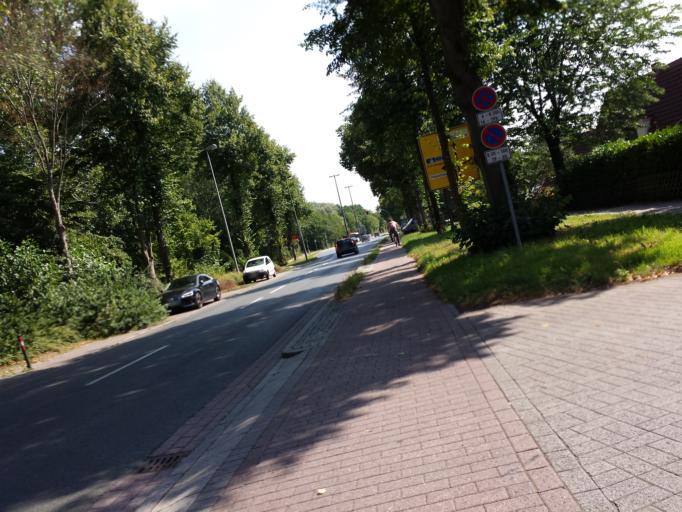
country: DE
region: Bremen
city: Bremen
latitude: 53.0388
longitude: 8.8354
